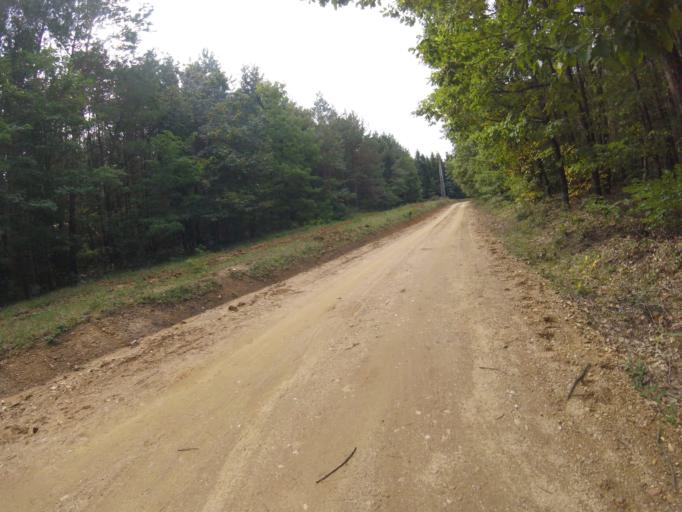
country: HU
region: Vas
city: Koszeg
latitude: 47.4050
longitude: 16.5750
